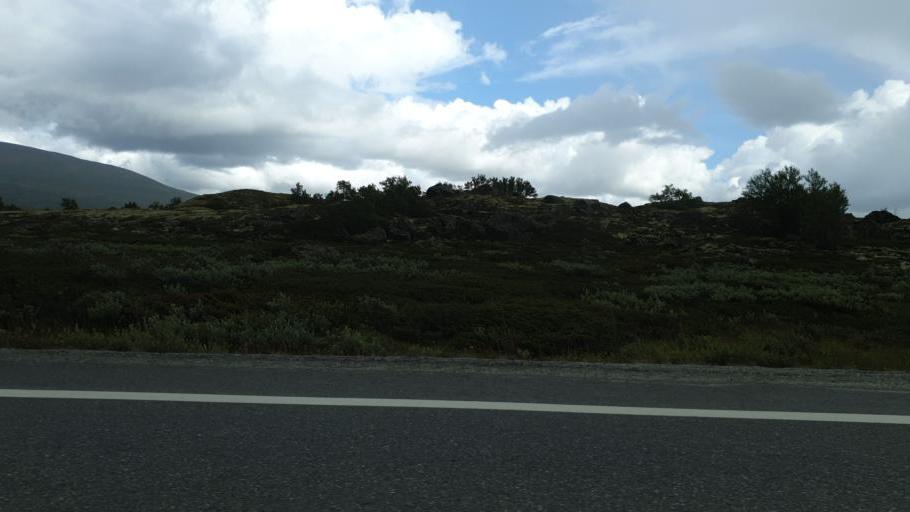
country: NO
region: Sor-Trondelag
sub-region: Oppdal
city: Oppdal
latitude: 62.2689
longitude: 9.5837
